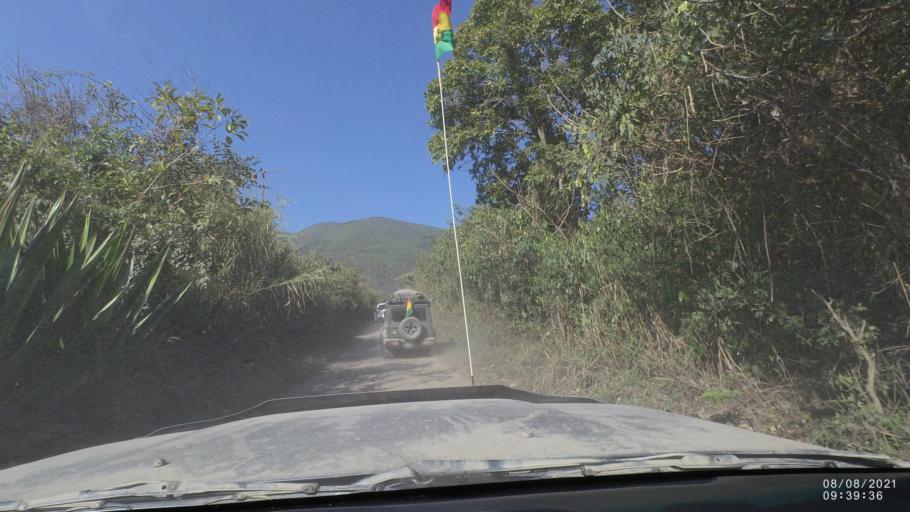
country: BO
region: La Paz
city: Quime
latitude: -16.5951
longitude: -66.7123
